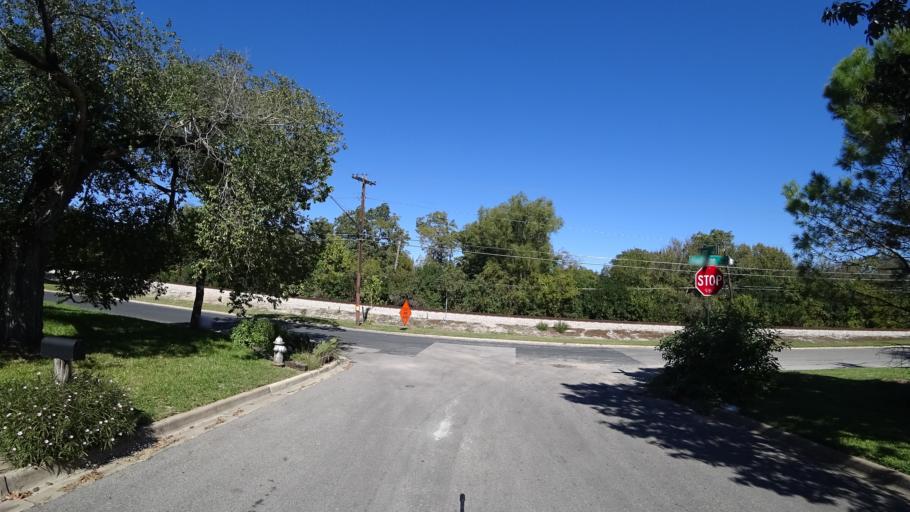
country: US
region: Texas
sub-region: Travis County
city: Austin
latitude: 30.2886
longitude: -97.7131
